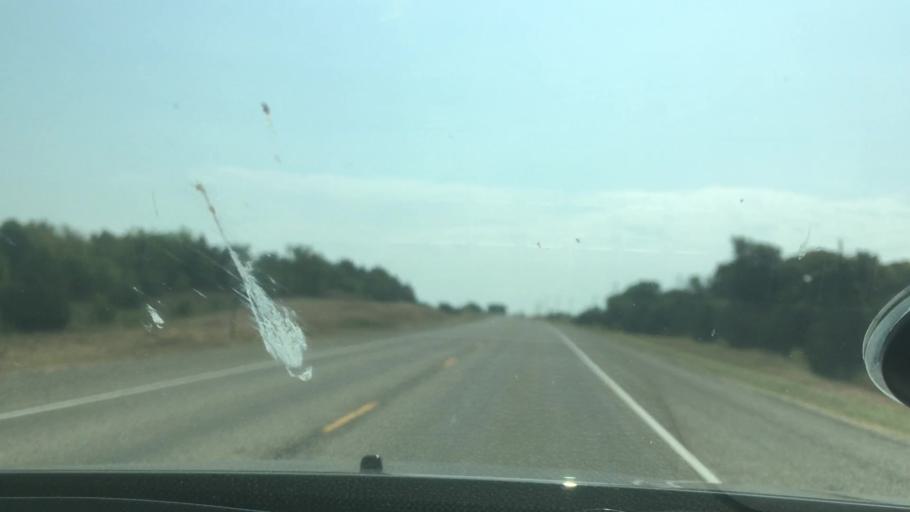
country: US
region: Texas
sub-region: Grayson County
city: Pottsboro
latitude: 33.8019
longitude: -96.6636
